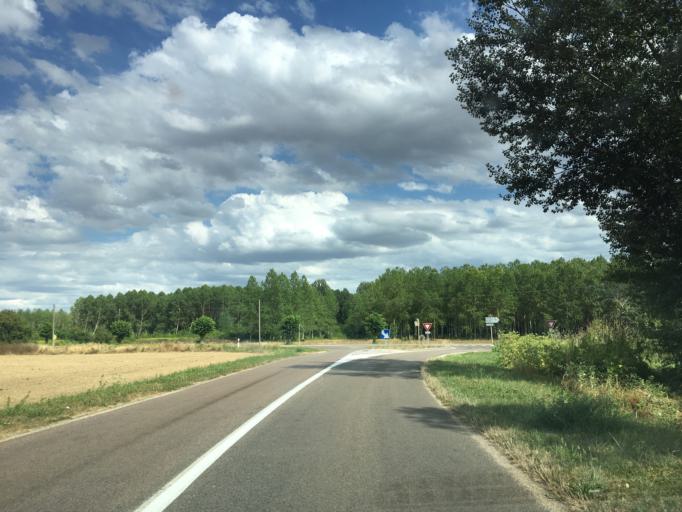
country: FR
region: Bourgogne
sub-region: Departement de l'Yonne
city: Joigny
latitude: 47.9685
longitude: 3.3858
